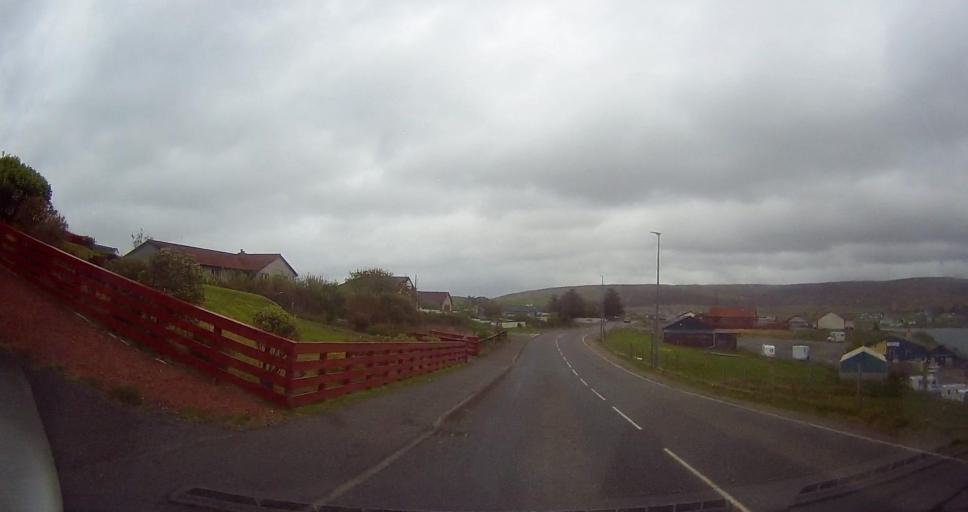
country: GB
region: Scotland
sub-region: Shetland Islands
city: Lerwick
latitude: 60.3926
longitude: -1.3683
